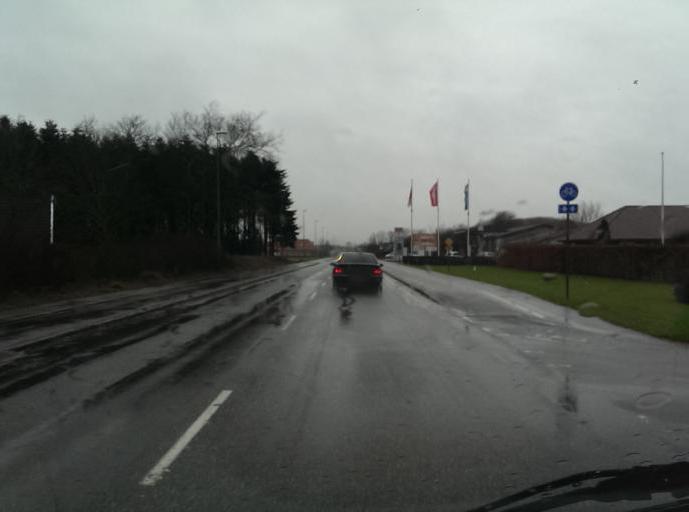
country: DK
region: South Denmark
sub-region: Varde Kommune
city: Olgod
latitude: 55.7166
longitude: 8.6107
